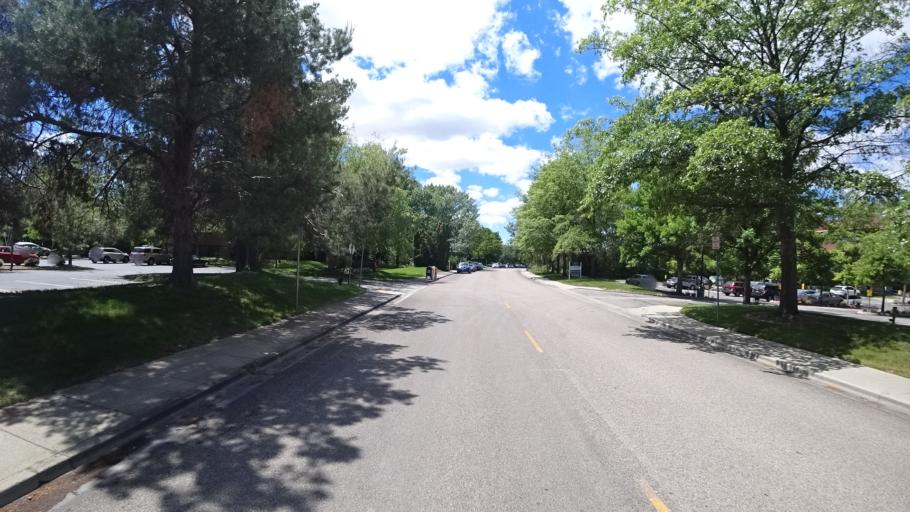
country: US
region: Idaho
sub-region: Ada County
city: Boise
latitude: 43.5961
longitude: -116.1795
